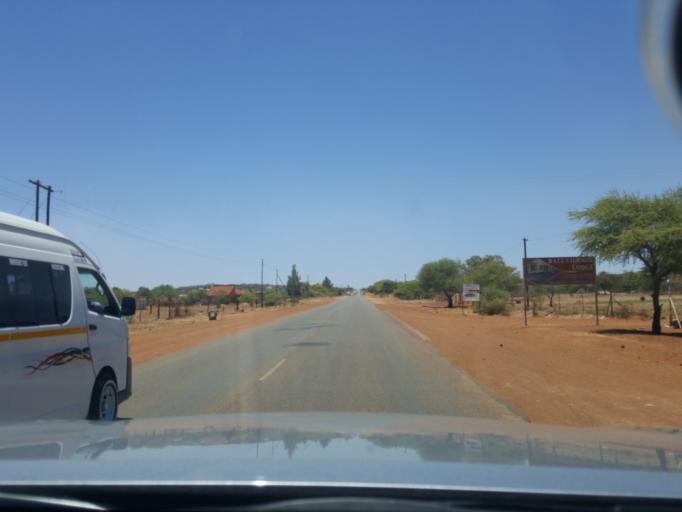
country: ZA
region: North-West
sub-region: Ngaka Modiri Molema District Municipality
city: Zeerust
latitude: -25.4447
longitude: 25.9651
